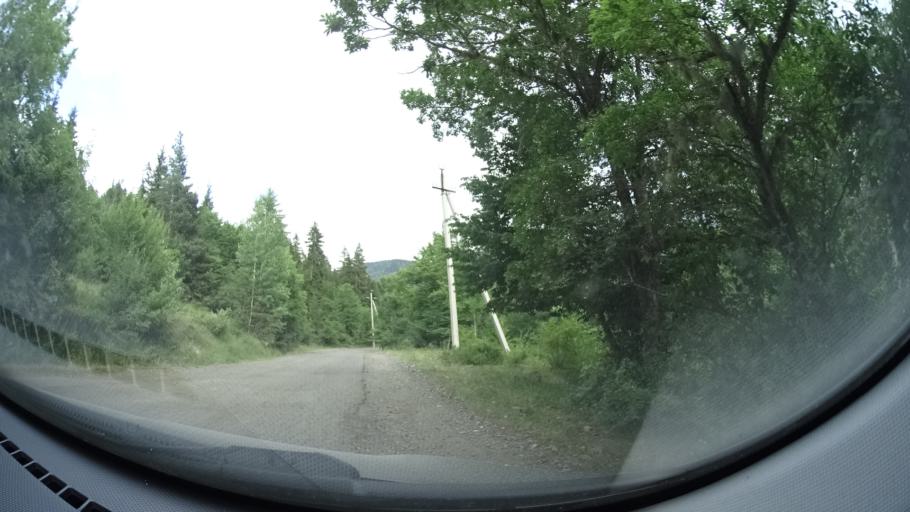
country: GE
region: Samtskhe-Javakheti
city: Adigeni
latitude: 41.6673
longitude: 42.6180
